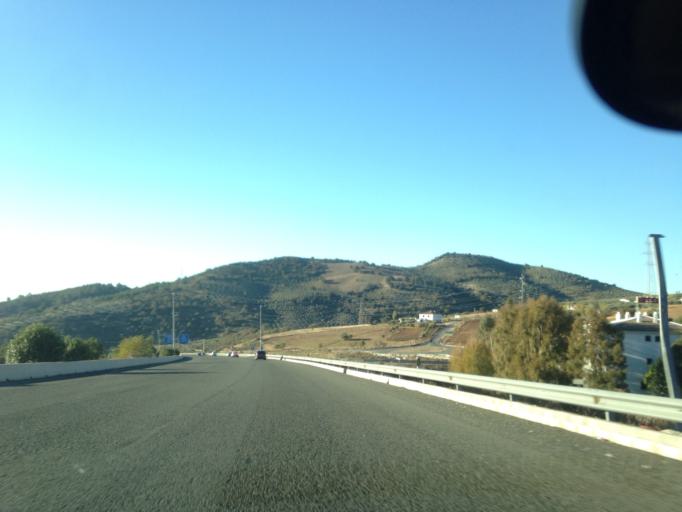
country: ES
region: Andalusia
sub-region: Provincia de Malaga
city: Casabermeja
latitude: 36.9620
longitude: -4.4464
